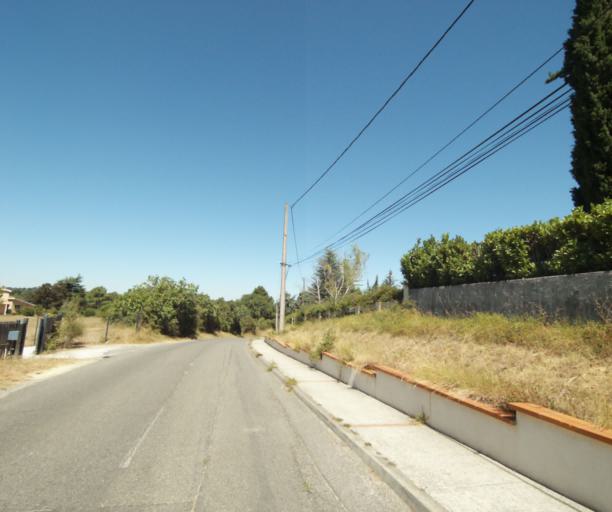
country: FR
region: Midi-Pyrenees
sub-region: Departement de la Haute-Garonne
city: Castanet-Tolosan
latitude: 43.5079
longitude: 1.4991
